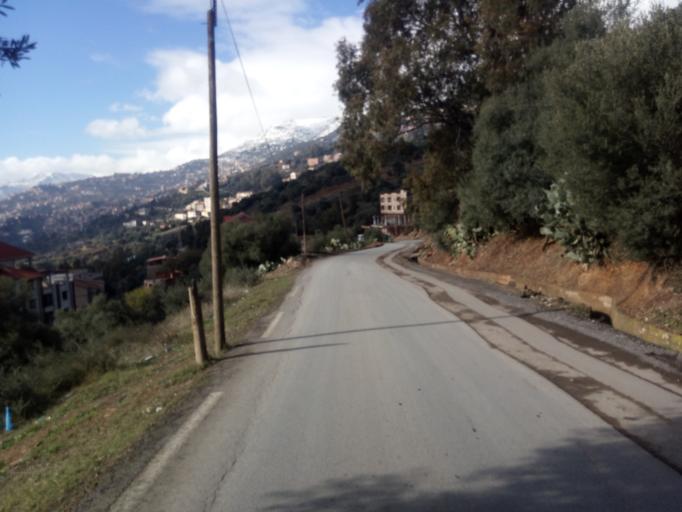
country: DZ
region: Tizi Ouzou
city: Chemini
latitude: 36.6080
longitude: 4.6481
